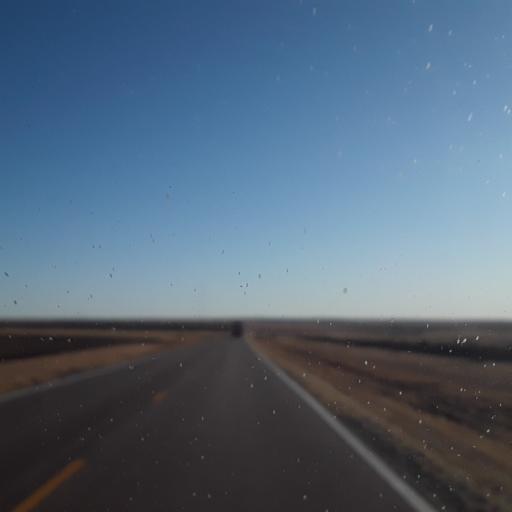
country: US
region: Kansas
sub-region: Wallace County
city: Sharon Springs
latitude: 39.1221
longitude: -101.7280
